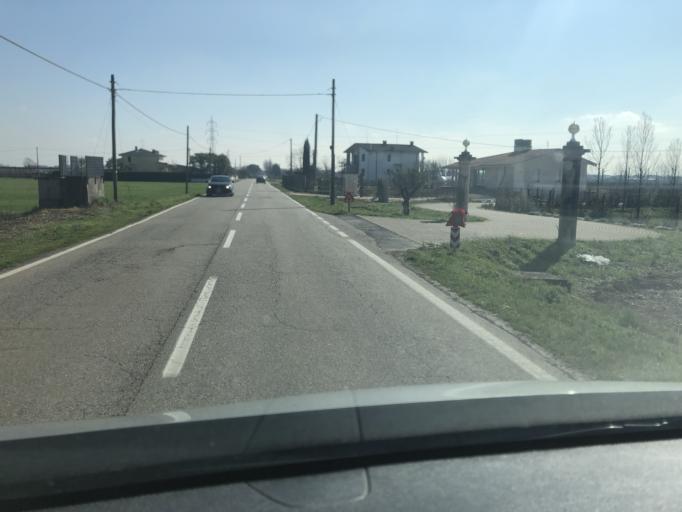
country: IT
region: Veneto
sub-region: Provincia di Verona
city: Villafranca di Verona
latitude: 45.3703
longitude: 10.8324
